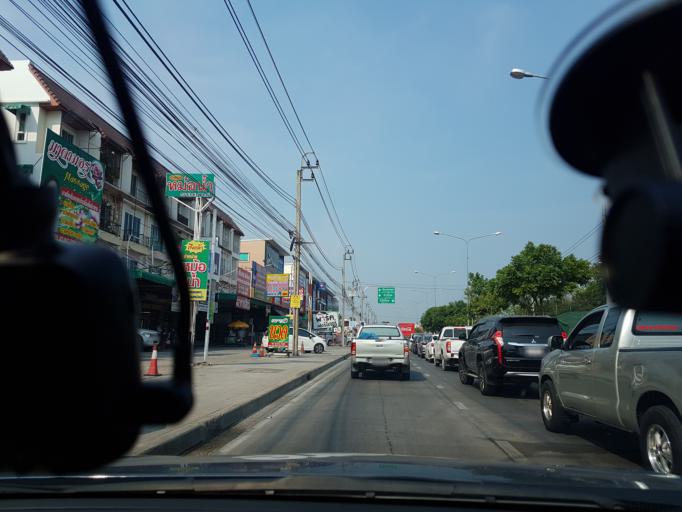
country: TH
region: Bangkok
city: Khlong Sam Wa
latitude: 13.8573
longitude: 100.7220
